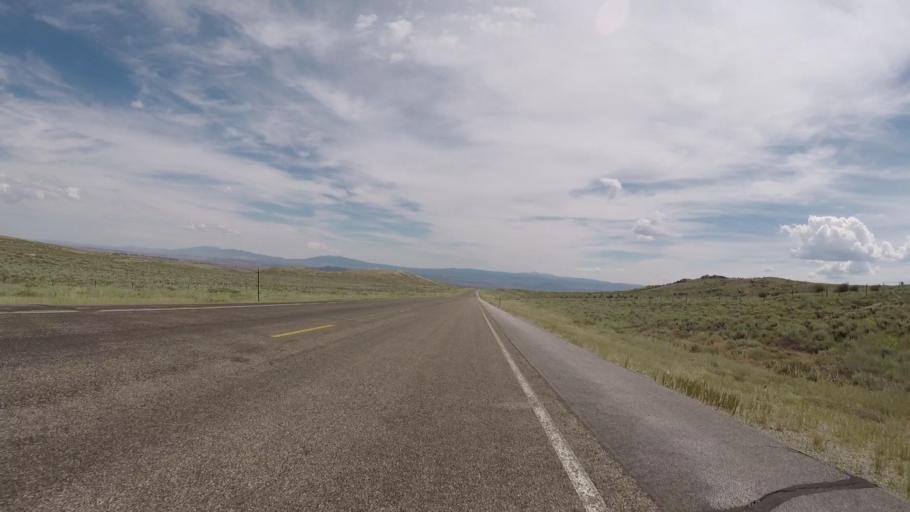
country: US
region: Wyoming
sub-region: Carbon County
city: Saratoga
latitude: 41.1983
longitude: -106.8389
